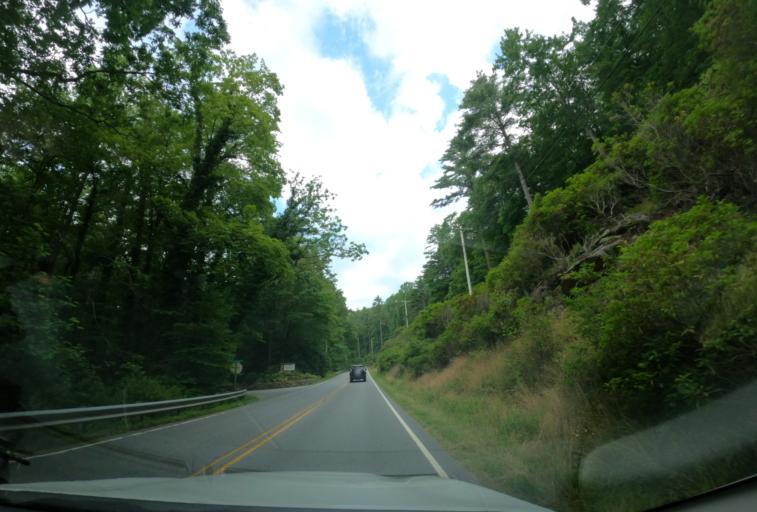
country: US
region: North Carolina
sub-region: Jackson County
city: Cullowhee
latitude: 35.1078
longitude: -83.1212
